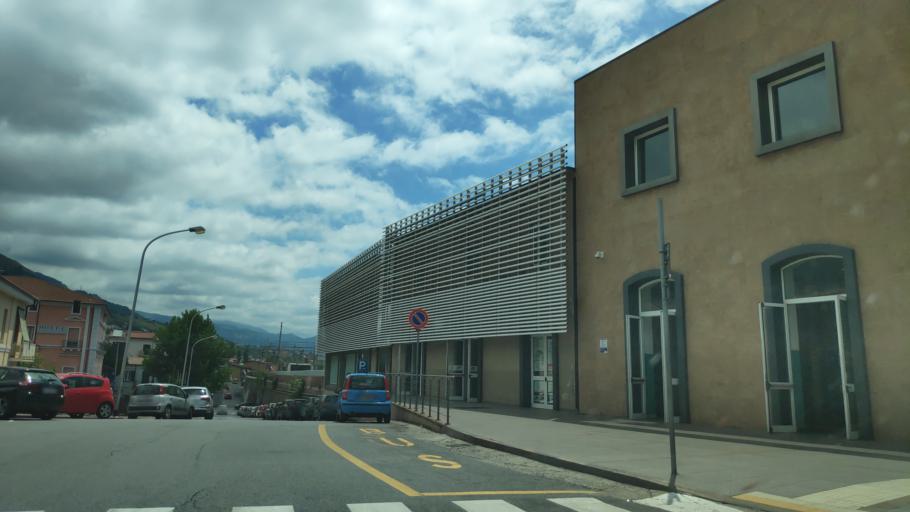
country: IT
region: Calabria
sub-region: Provincia di Cosenza
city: Paola
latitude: 39.3595
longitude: 16.0336
